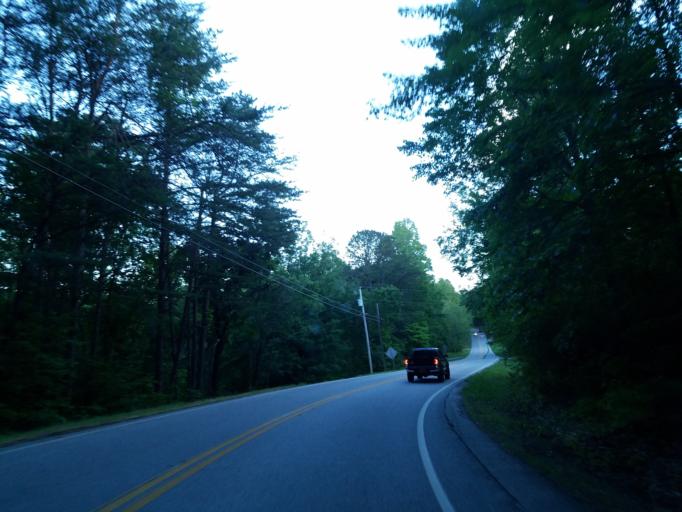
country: US
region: Georgia
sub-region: Lumpkin County
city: Dahlonega
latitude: 34.5998
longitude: -83.9697
